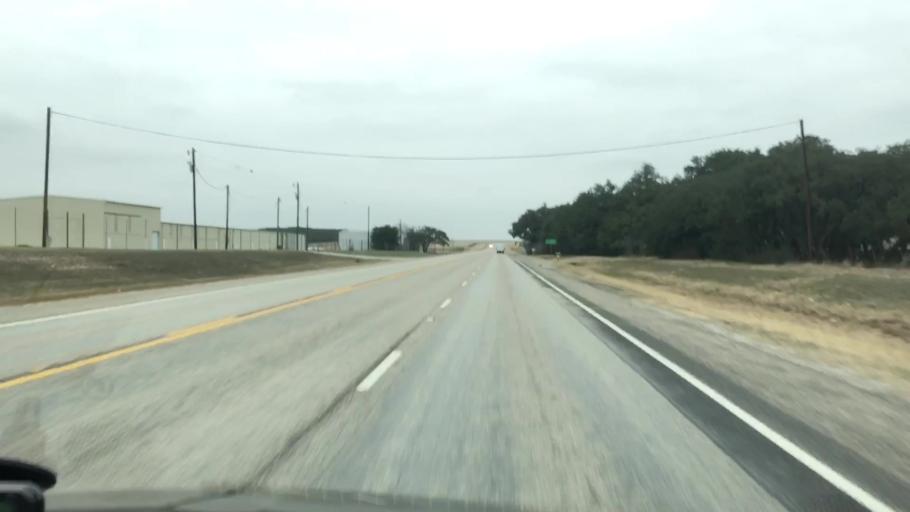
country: US
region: Texas
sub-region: Lampasas County
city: Lampasas
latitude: 31.1004
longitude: -98.1926
